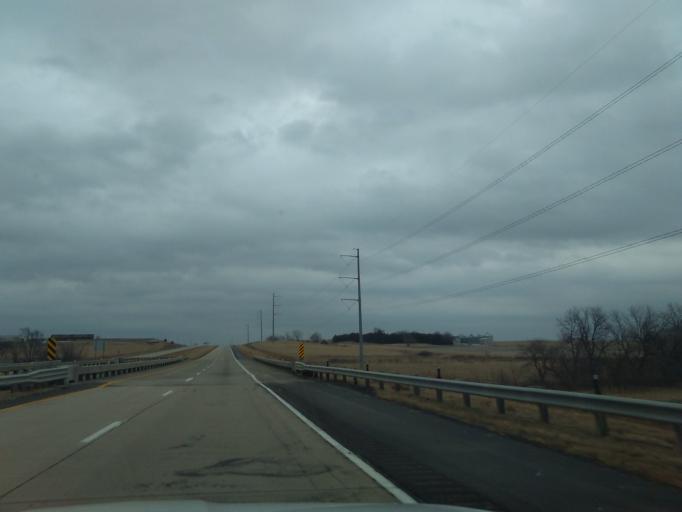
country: US
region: Nebraska
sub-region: Otoe County
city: Syracuse
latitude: 40.6701
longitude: -96.1667
